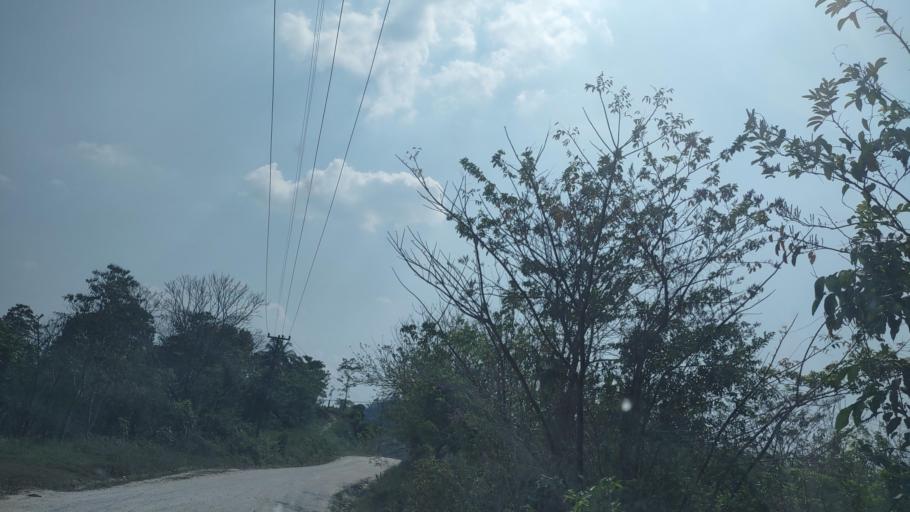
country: MX
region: Tabasco
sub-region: Huimanguillo
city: Francisco Rueda
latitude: 17.5653
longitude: -93.8869
